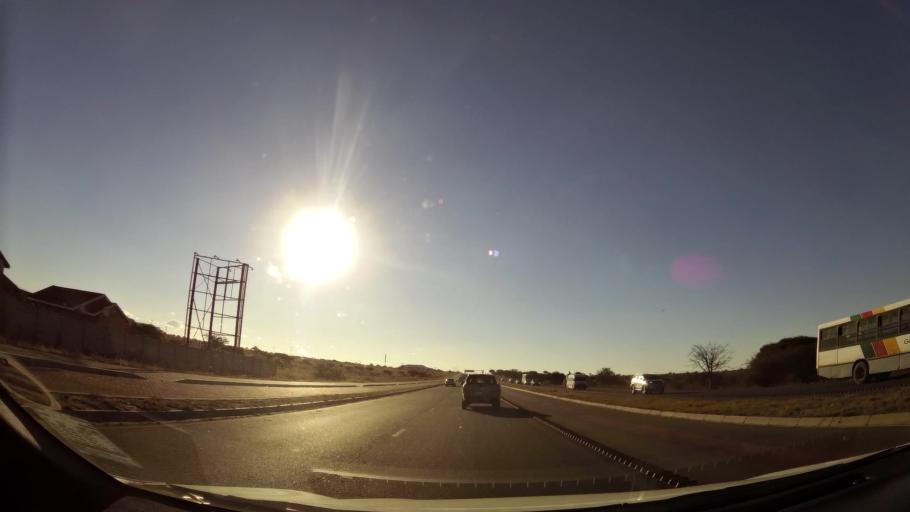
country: ZA
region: Limpopo
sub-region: Capricorn District Municipality
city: Polokwane
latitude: -23.8706
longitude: 29.4130
